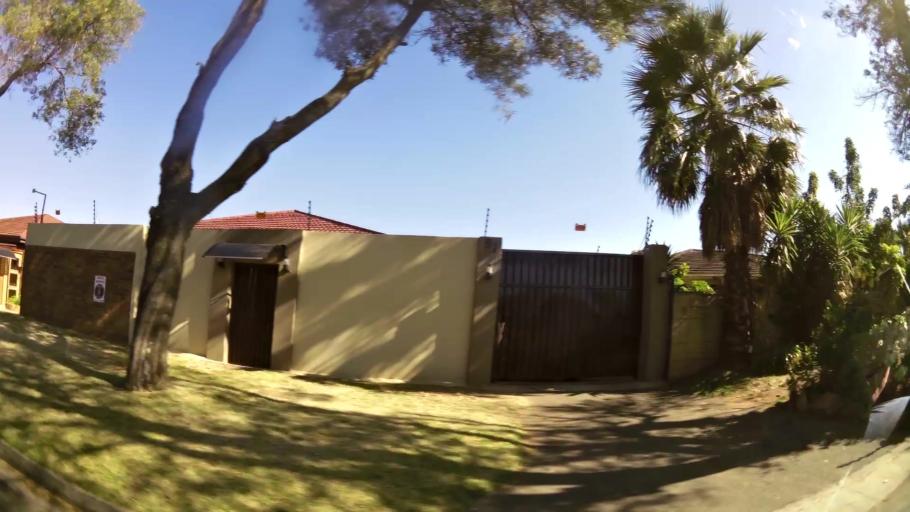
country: ZA
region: Gauteng
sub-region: City of Johannesburg Metropolitan Municipality
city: Johannesburg
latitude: -26.1896
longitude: 27.9833
